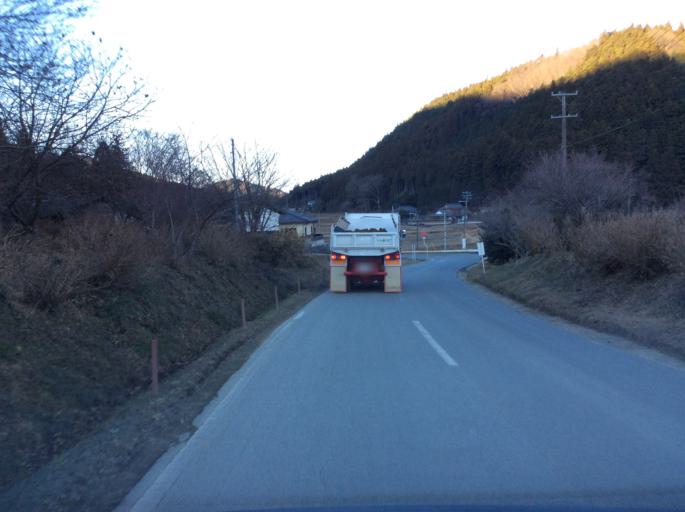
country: JP
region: Ibaraki
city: Kitaibaraki
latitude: 36.8839
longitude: 140.7219
